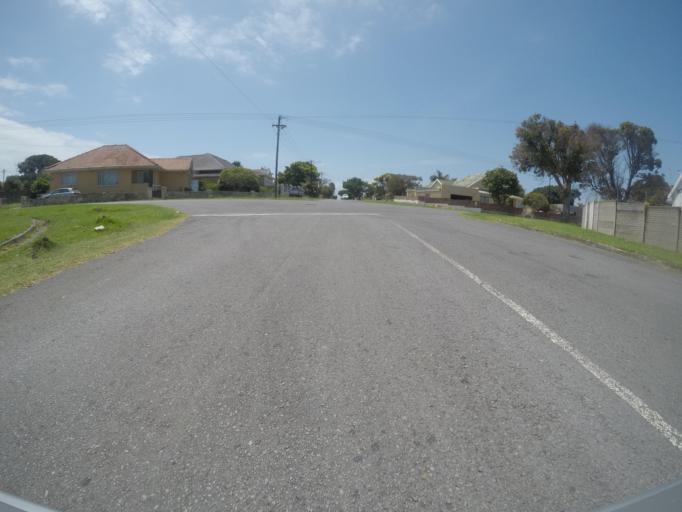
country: ZA
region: Eastern Cape
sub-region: Buffalo City Metropolitan Municipality
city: East London
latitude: -32.9760
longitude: 27.8803
